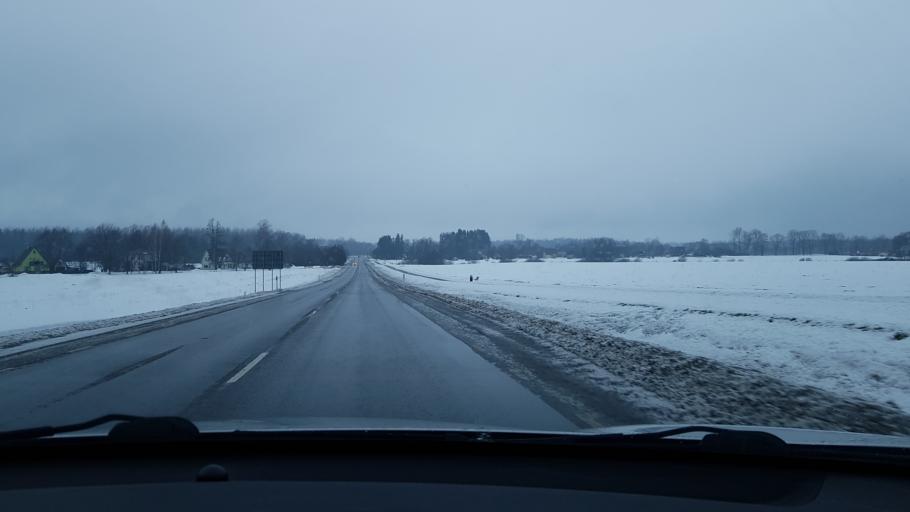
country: EE
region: Jaervamaa
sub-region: Tueri vald
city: Tueri
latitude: 58.8148
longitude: 25.4002
